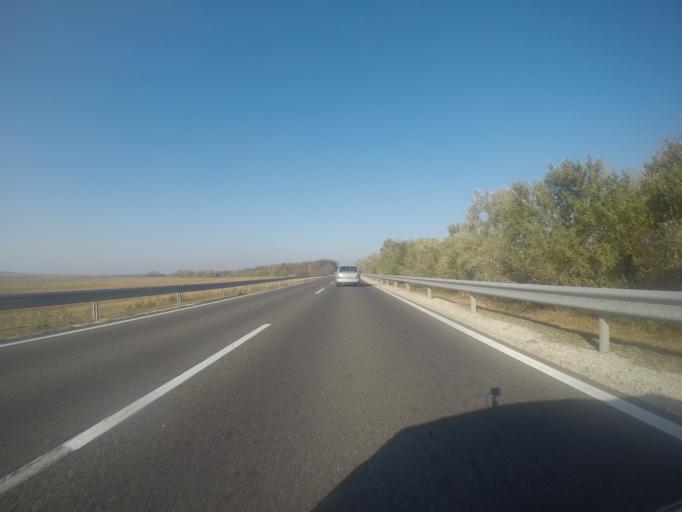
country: HU
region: Fejer
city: Ivancsa
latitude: 47.1647
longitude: 18.8638
